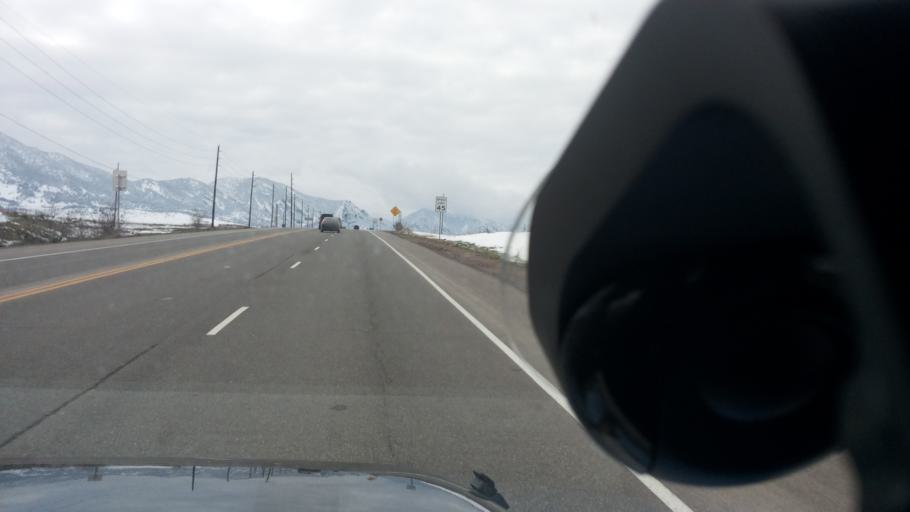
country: US
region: Colorado
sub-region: Jefferson County
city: Golden
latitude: 39.8596
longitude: -105.2350
